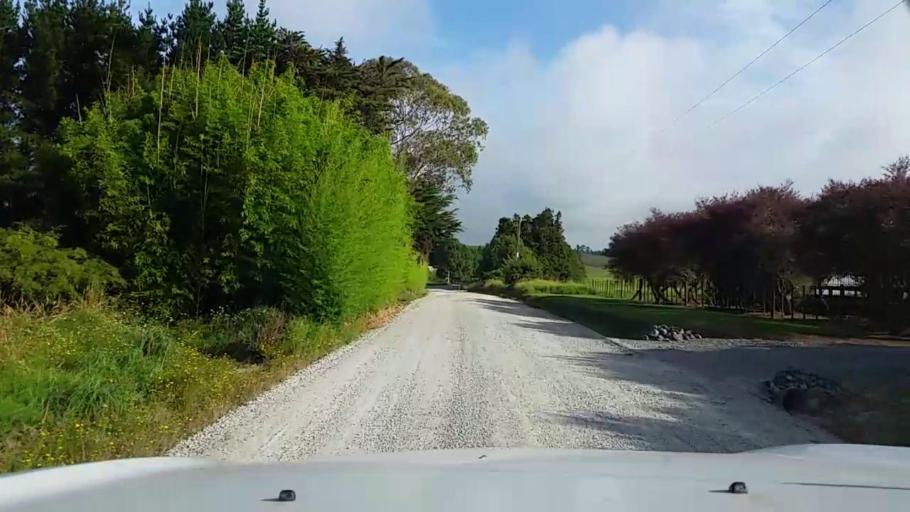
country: NZ
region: Northland
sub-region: Whangarei
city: Maungatapere
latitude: -35.6816
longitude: 174.1788
